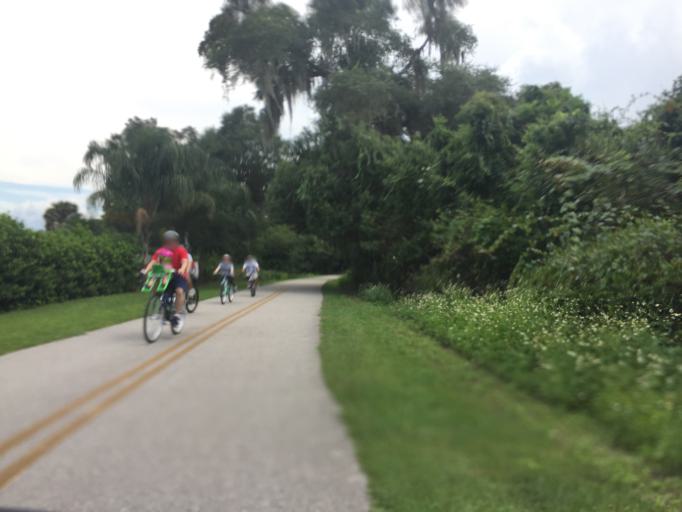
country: US
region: Florida
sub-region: Seminole County
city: Oviedo
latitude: 28.6760
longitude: -81.2125
